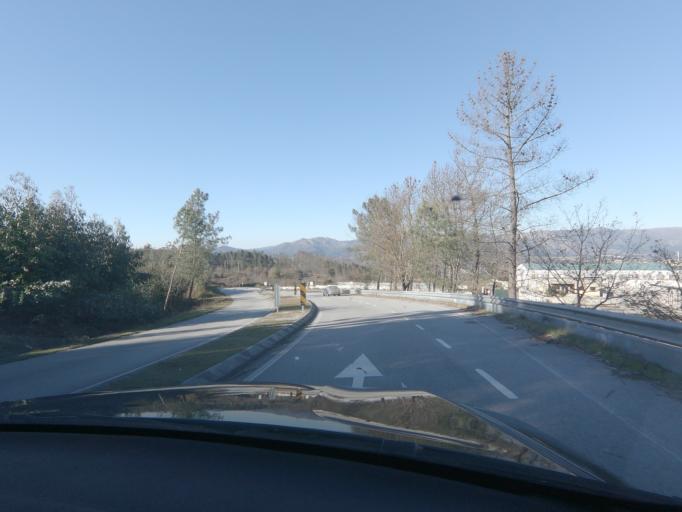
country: PT
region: Viseu
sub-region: Vouzela
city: Vouzela
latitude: 40.7207
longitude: -8.1309
